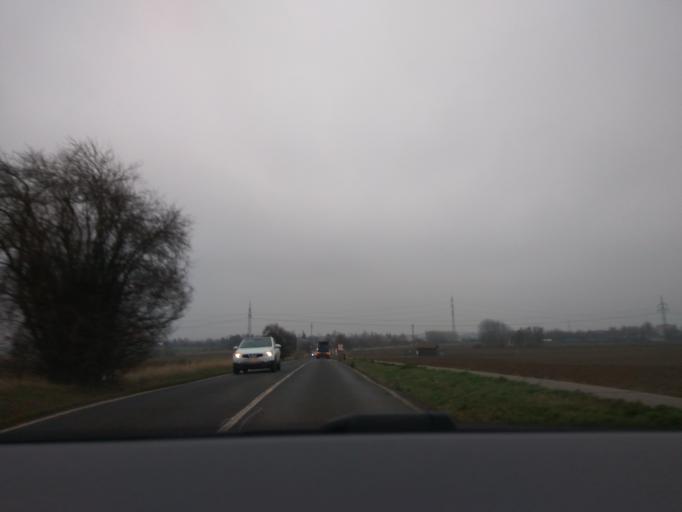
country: CZ
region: Central Bohemia
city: Hovorcovice
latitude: 50.1727
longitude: 14.5201
